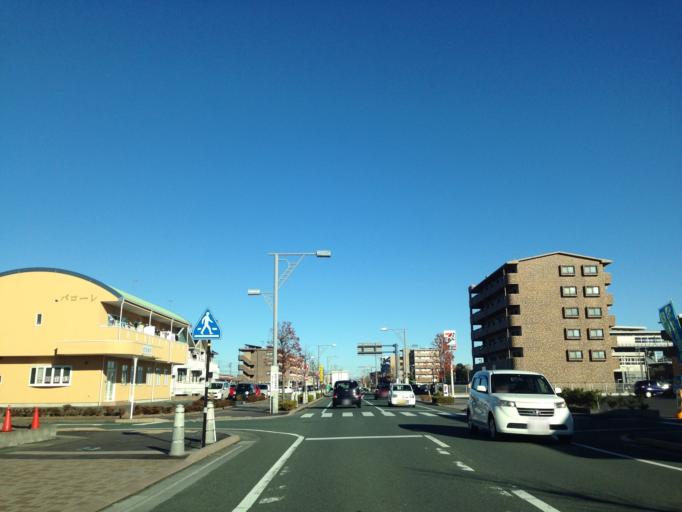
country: JP
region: Shizuoka
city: Fukuroi
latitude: 34.7524
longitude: 137.9590
